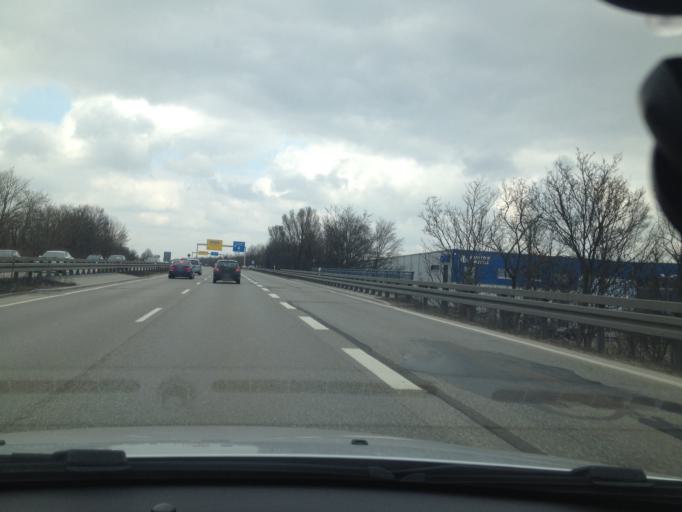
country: DE
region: Bavaria
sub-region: Swabia
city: Gersthofen
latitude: 48.4107
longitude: 10.8735
